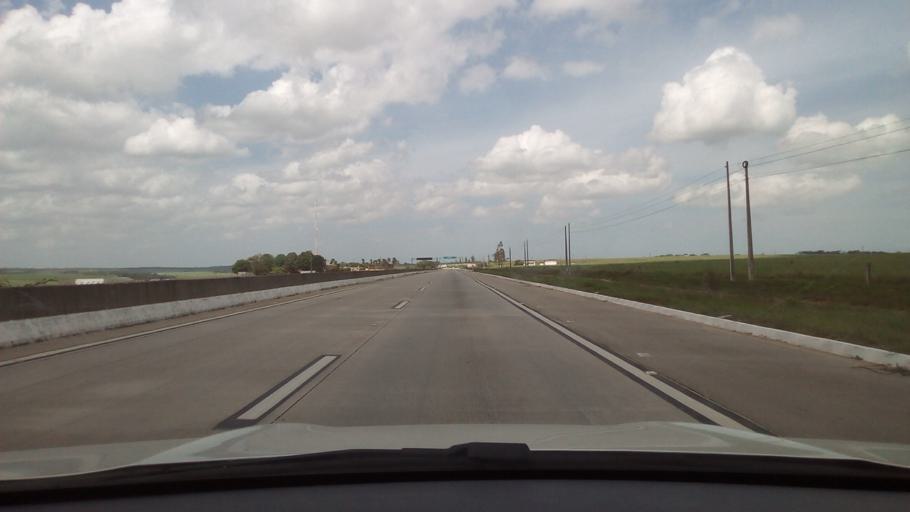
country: BR
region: Paraiba
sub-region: Mamanguape
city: Mamanguape
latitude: -6.8000
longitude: -35.1389
